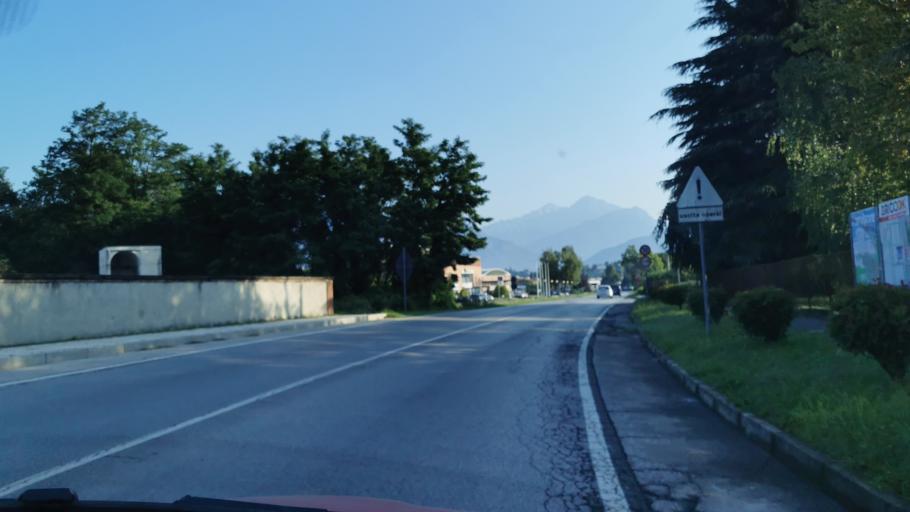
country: IT
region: Lombardy
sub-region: Provincia di Lecco
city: Dolzago
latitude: 45.7724
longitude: 9.3387
